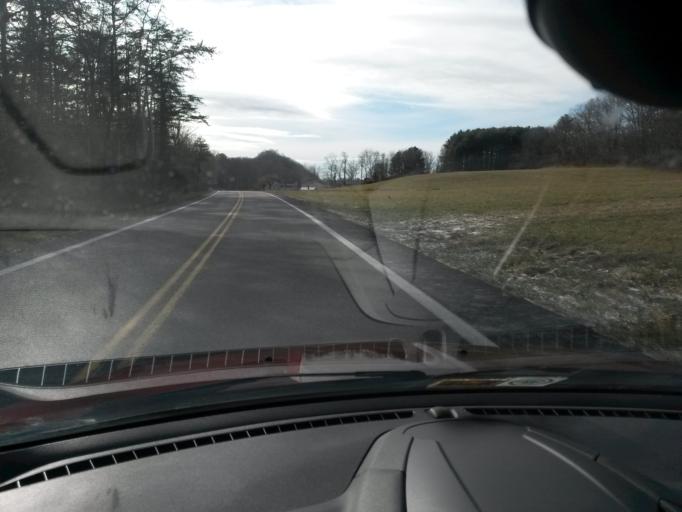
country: US
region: Virginia
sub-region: Augusta County
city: Jolivue
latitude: 38.1148
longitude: -79.2951
